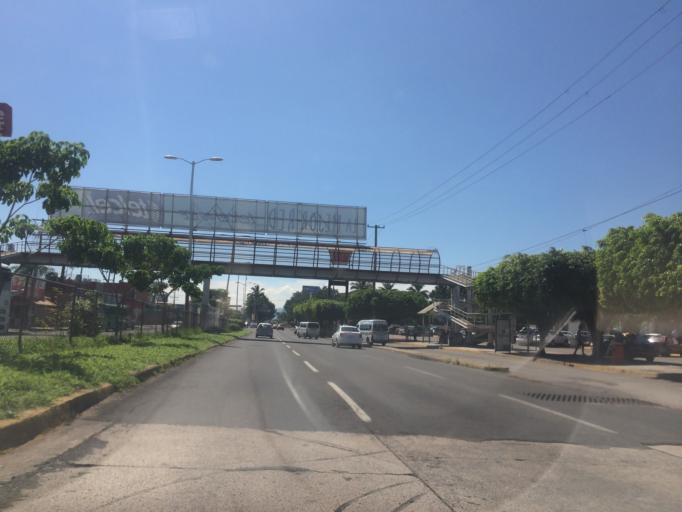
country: MX
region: Nayarit
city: Tepic
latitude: 21.4944
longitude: -104.8825
